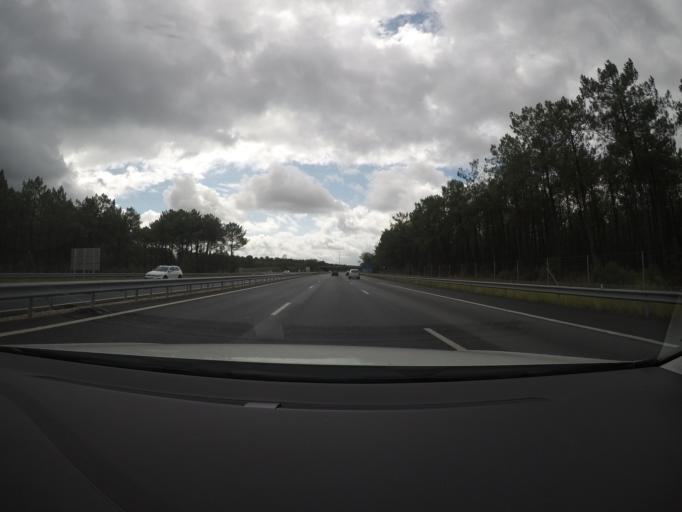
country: FR
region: Aquitaine
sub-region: Departement de la Gironde
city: Belin-Beliet
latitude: 44.4511
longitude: -0.8104
